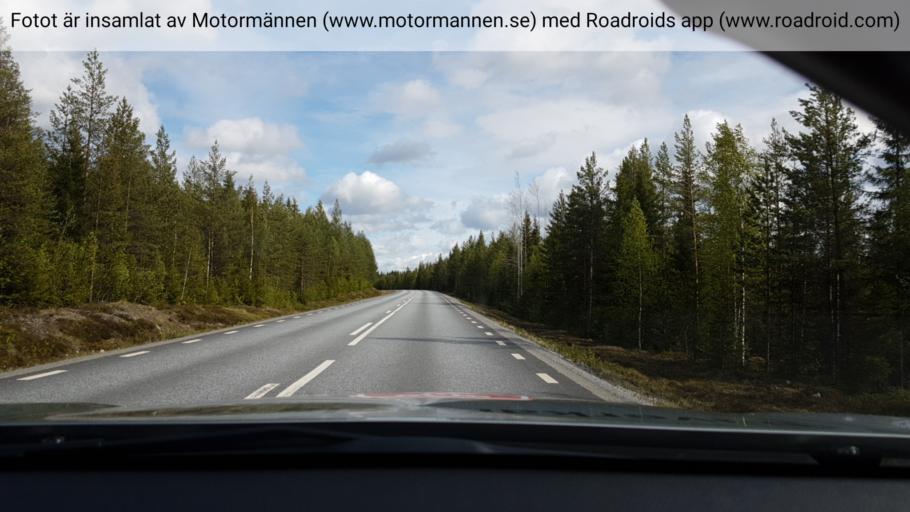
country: SE
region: Vaesterbotten
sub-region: Lycksele Kommun
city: Lycksele
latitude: 64.0753
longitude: 18.3468
